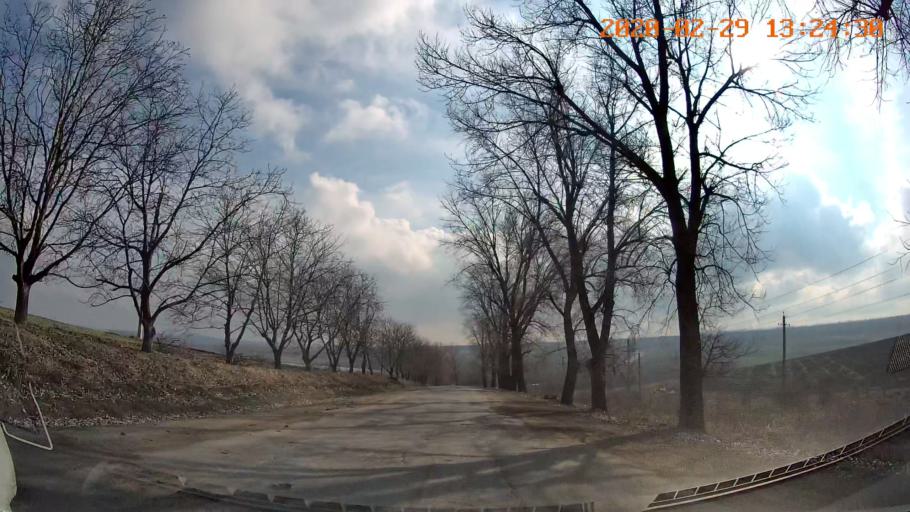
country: MD
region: Telenesti
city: Camenca
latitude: 47.9381
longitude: 28.6278
